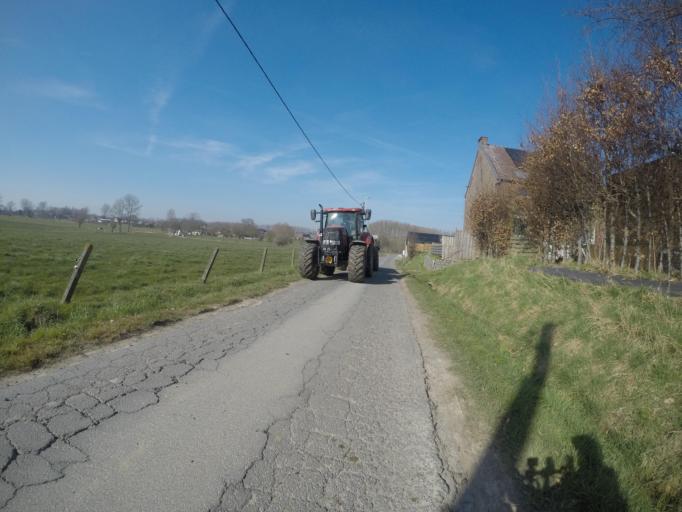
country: BE
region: Flanders
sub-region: Provincie Oost-Vlaanderen
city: Sint-Maria-Lierde
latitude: 50.7860
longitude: 3.8138
